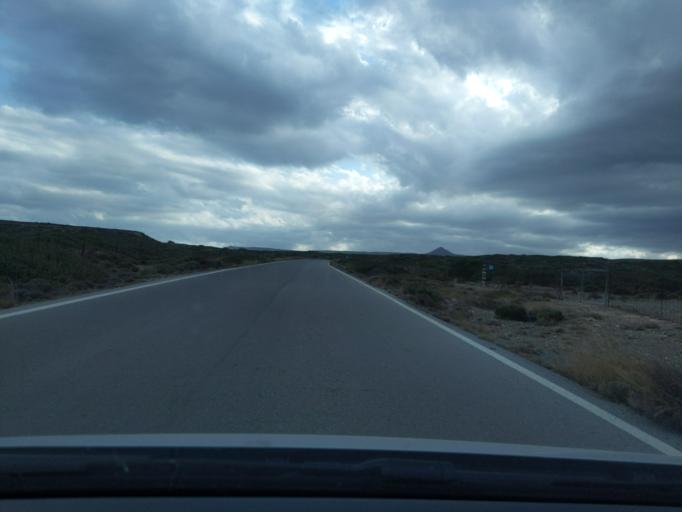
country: GR
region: Crete
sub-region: Nomos Lasithiou
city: Palekastro
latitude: 35.2464
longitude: 26.2499
